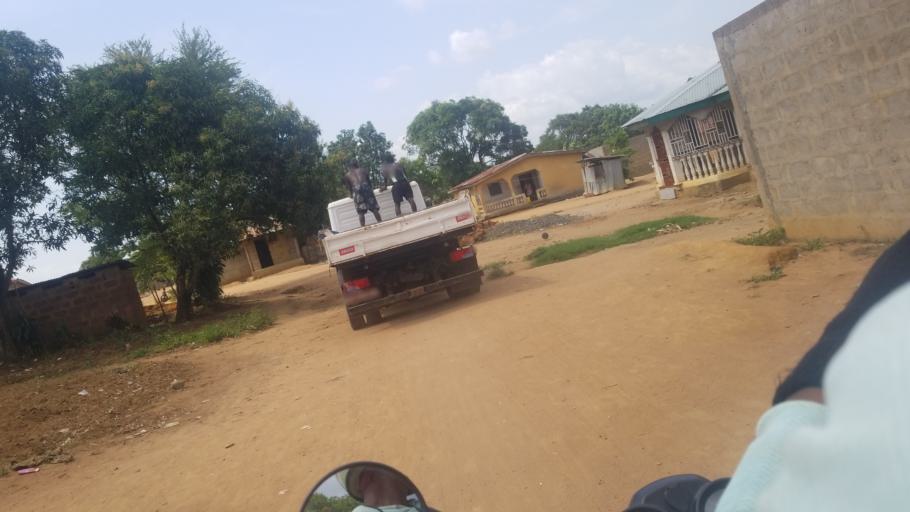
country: SL
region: Western Area
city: Waterloo
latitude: 8.3171
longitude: -13.0447
